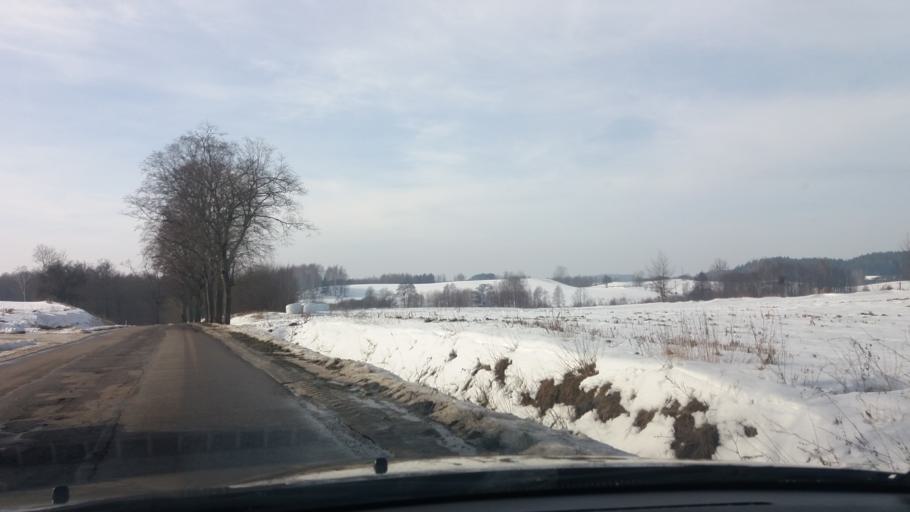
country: PL
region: Warmian-Masurian Voivodeship
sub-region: Powiat lidzbarski
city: Lidzbark Warminski
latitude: 54.1069
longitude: 20.6654
